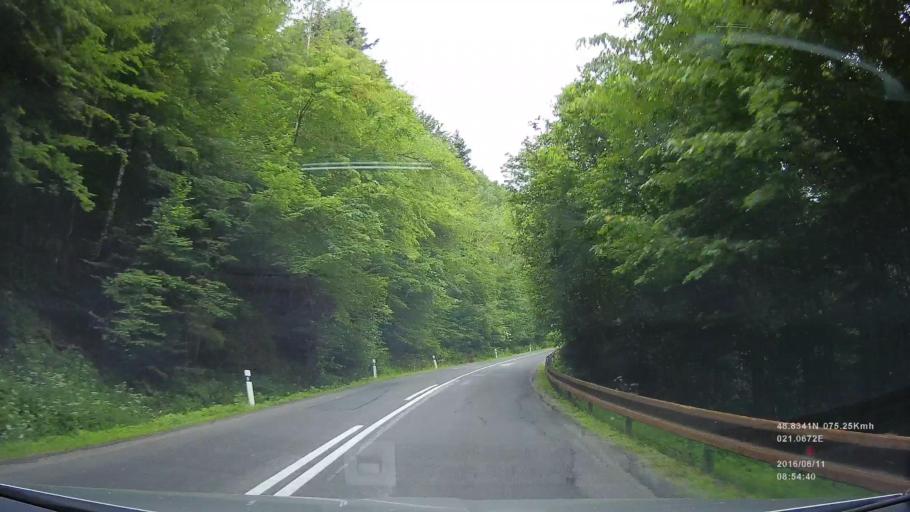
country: SK
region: Kosicky
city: Gelnica
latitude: 48.8333
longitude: 21.0728
